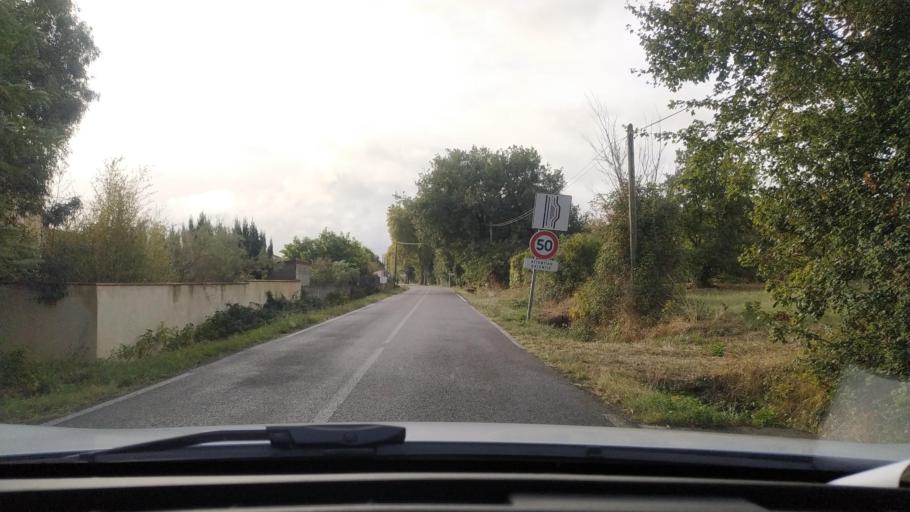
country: FR
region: Midi-Pyrenees
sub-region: Departement de la Haute-Garonne
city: Gaillac-Toulza
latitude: 43.3032
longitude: 1.4676
